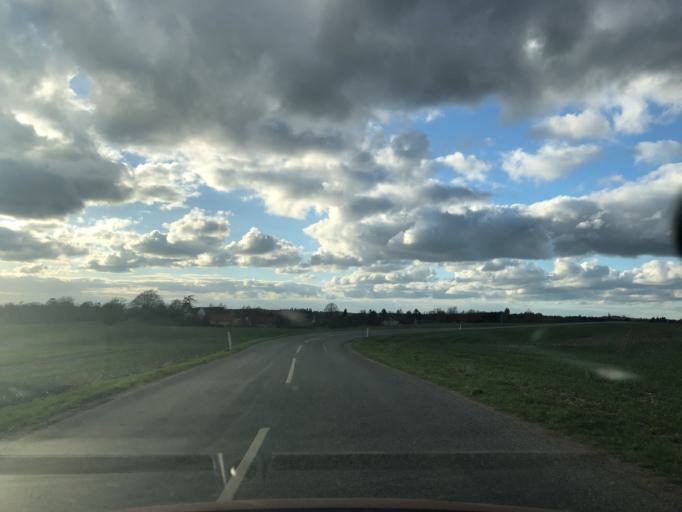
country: DK
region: Zealand
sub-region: Lejre Kommune
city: Kirke Hvalso
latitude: 55.5134
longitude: 11.8744
